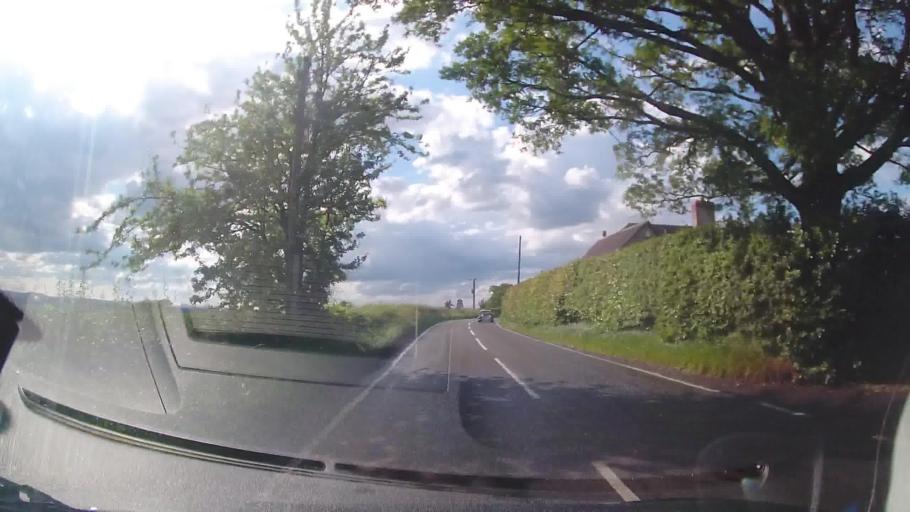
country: GB
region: England
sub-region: Shropshire
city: Harley
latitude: 52.6566
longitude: -2.6150
